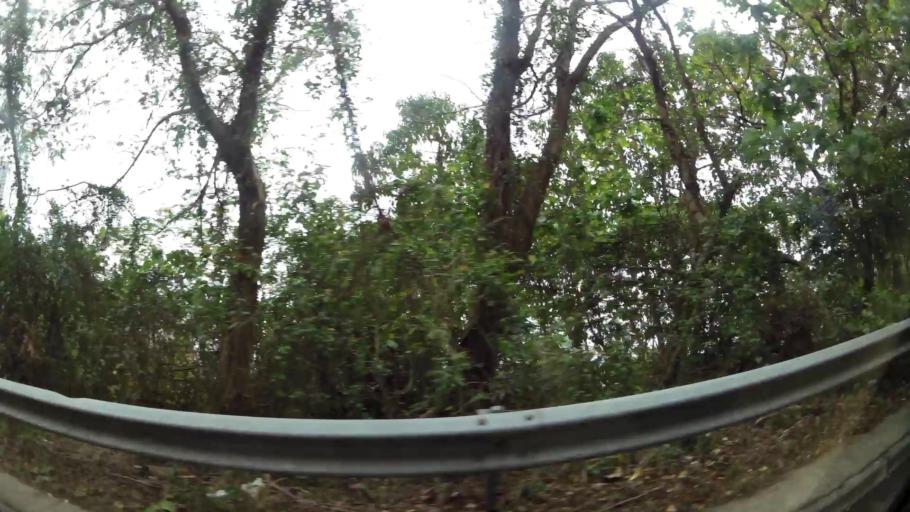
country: HK
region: Central and Western
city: Central
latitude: 22.2723
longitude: 114.1232
